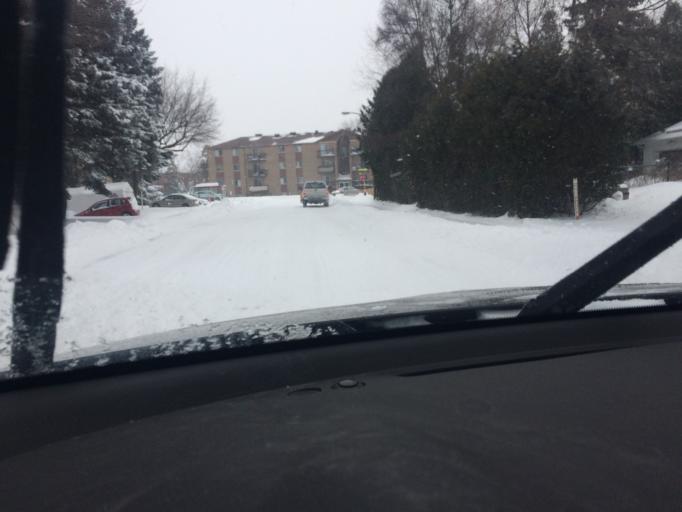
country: CA
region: Quebec
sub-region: Monteregie
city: Brossard
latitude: 45.4675
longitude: -73.4536
